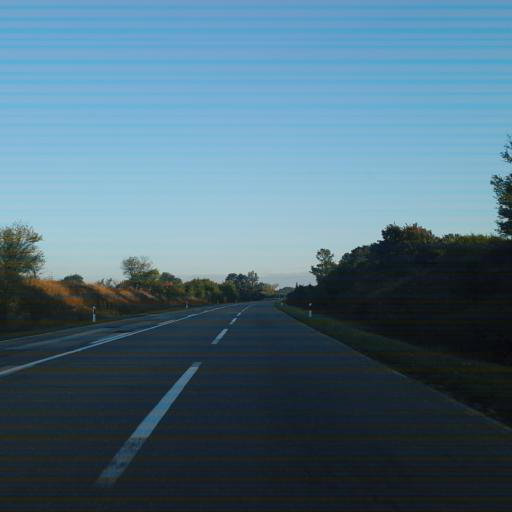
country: RS
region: Central Serbia
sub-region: Borski Okrug
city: Negotin
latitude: 44.1126
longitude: 22.3433
